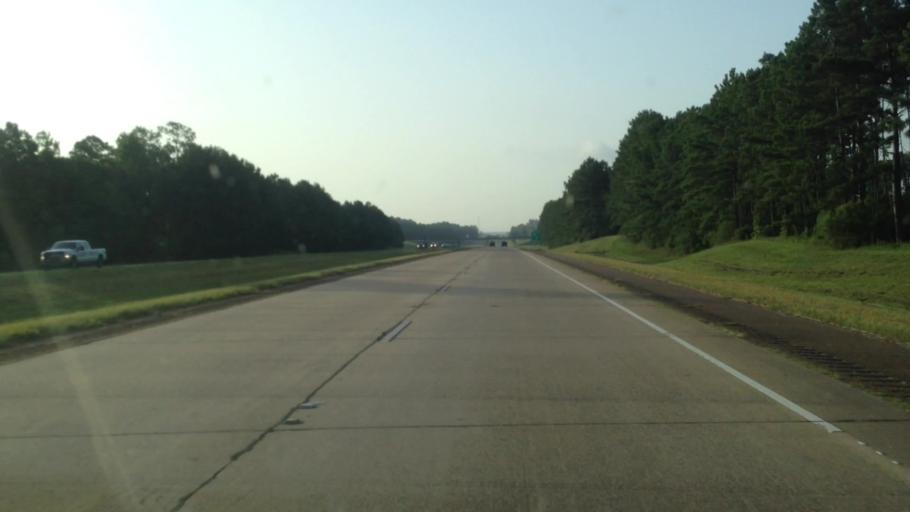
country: US
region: Louisiana
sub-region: Rapides Parish
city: Boyce
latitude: 31.4148
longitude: -92.7247
